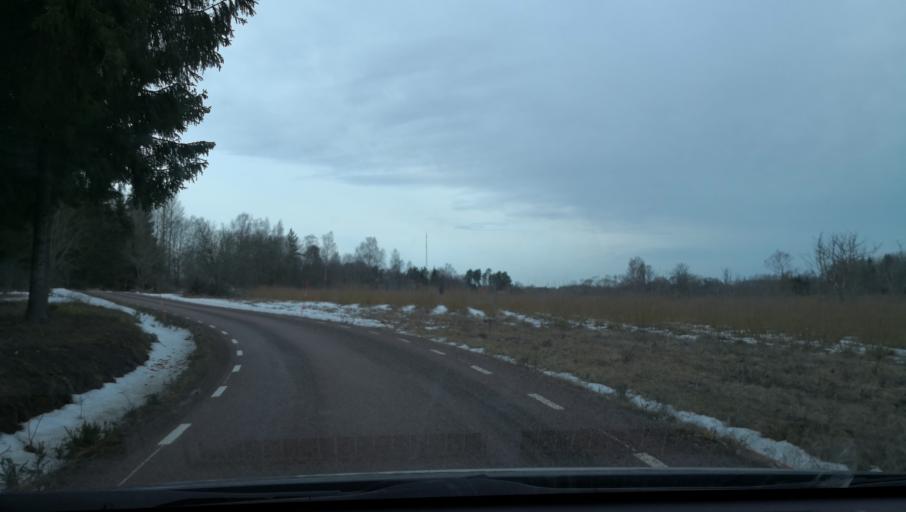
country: SE
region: Vaestmanland
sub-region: Vasteras
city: Skultuna
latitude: 59.6119
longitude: 16.4102
